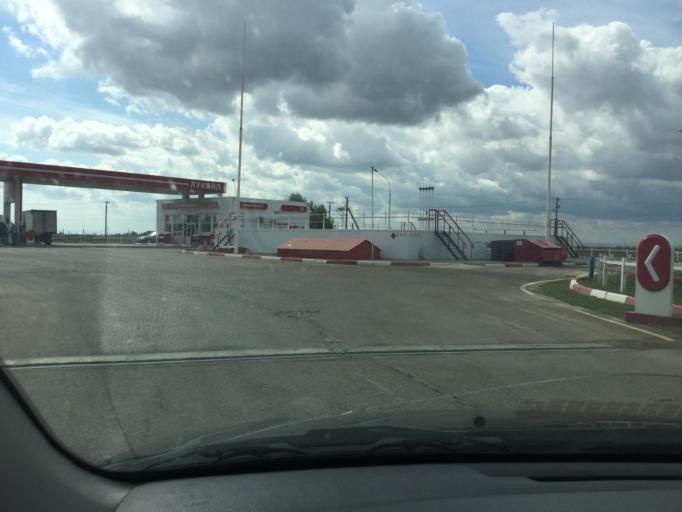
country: RU
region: Krasnodarskiy
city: Slavyansk-na-Kubani
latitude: 45.2475
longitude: 38.1008
